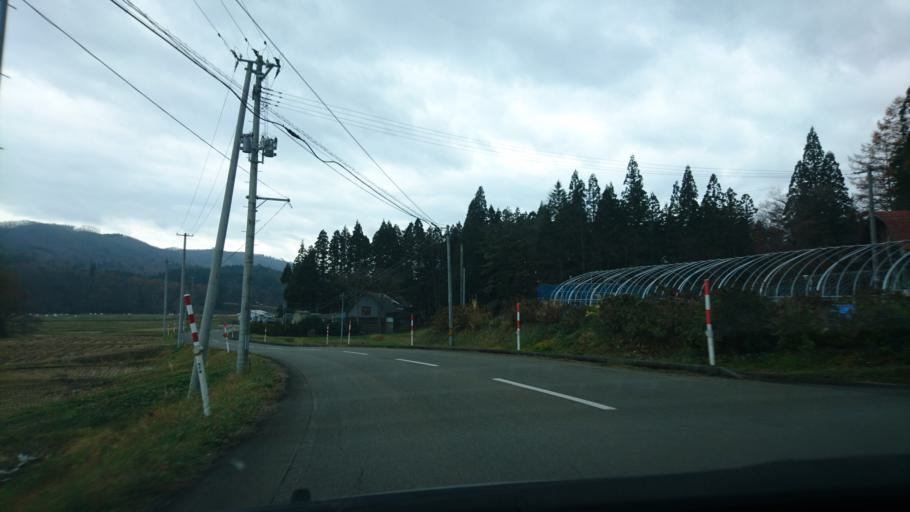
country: JP
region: Iwate
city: Ichinoseki
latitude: 38.9606
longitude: 140.9409
